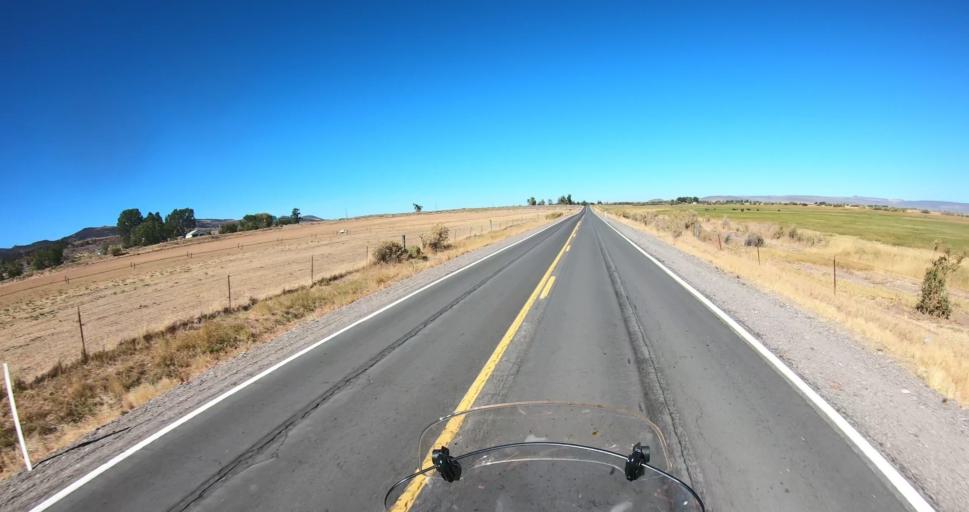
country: US
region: Oregon
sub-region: Lake County
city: Lakeview
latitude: 42.6679
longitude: -120.5240
